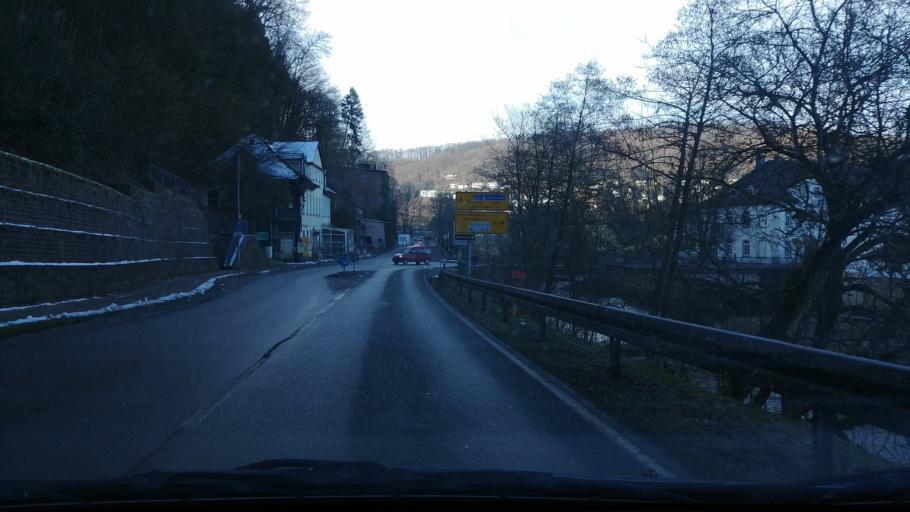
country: DE
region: Lower Saxony
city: Bad Karlshafen
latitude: 51.6401
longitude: 9.4495
